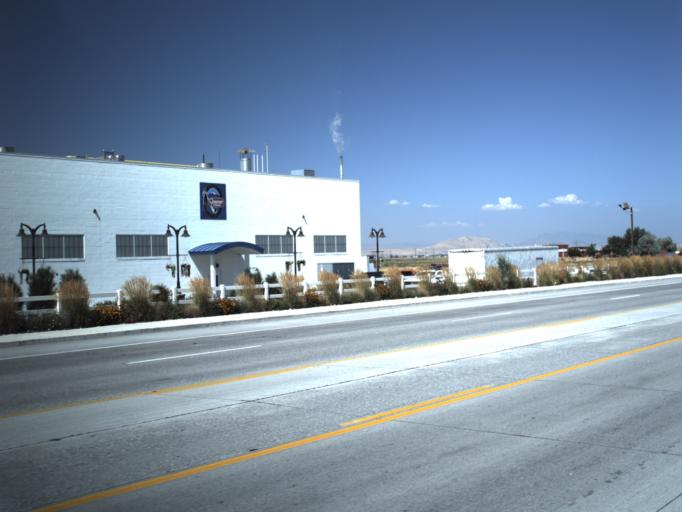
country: US
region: Utah
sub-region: Cache County
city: Logan
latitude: 41.7530
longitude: -111.8589
